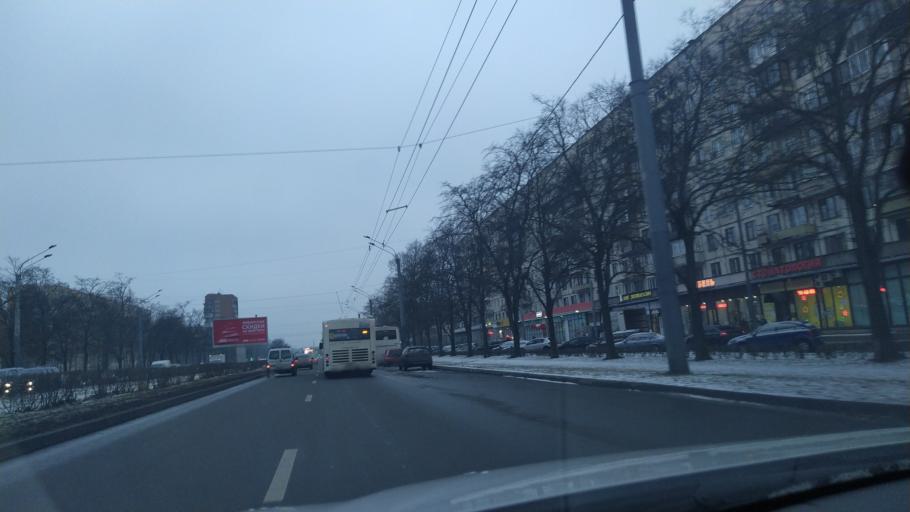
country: RU
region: St.-Petersburg
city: Grazhdanka
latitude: 60.0371
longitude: 30.3965
